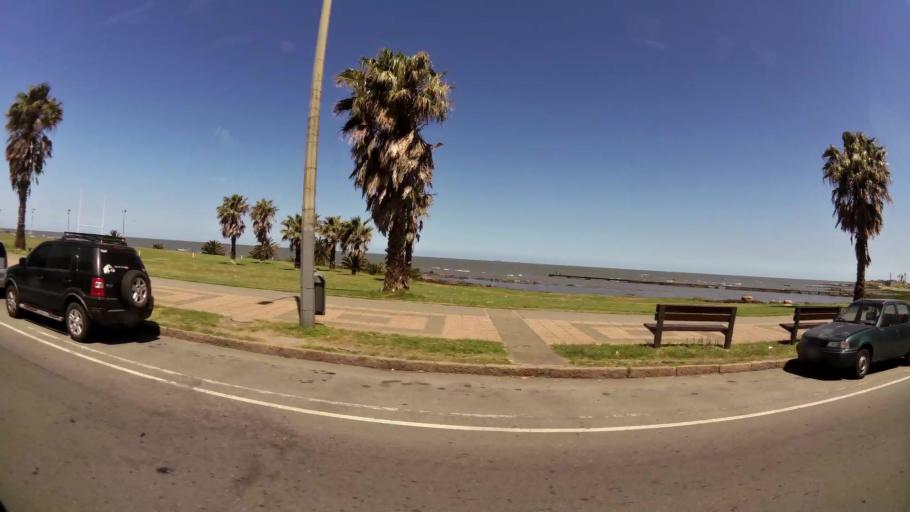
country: UY
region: Montevideo
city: Montevideo
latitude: -34.9269
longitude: -56.1575
